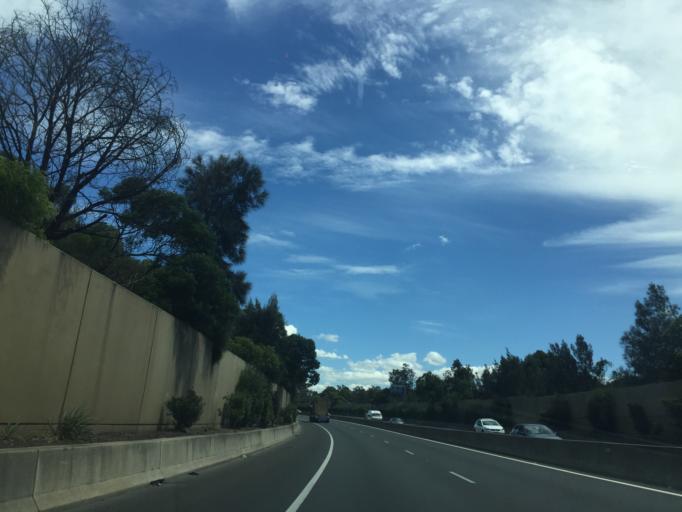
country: AU
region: New South Wales
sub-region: Canterbury
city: Clemton Park
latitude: -33.9402
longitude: 151.0867
